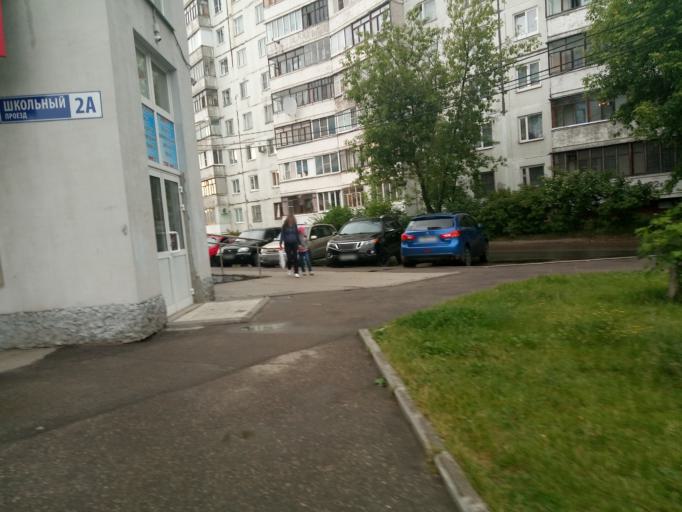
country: RU
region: Jaroslavl
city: Yaroslavl
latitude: 57.6511
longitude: 39.9593
